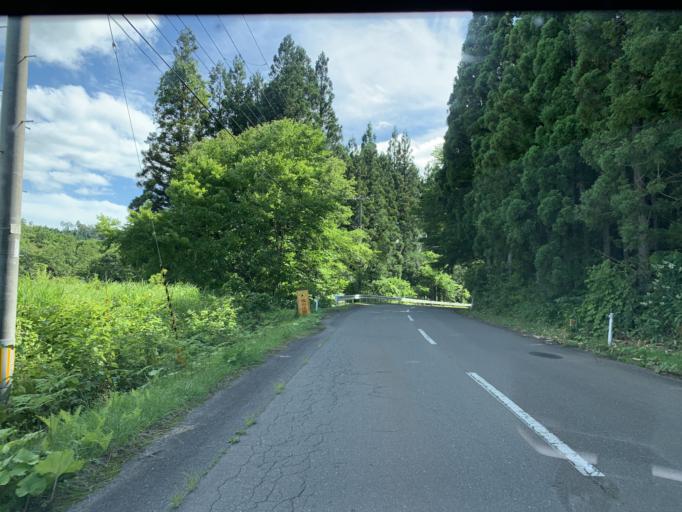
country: JP
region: Iwate
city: Ichinoseki
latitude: 38.9493
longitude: 140.9279
